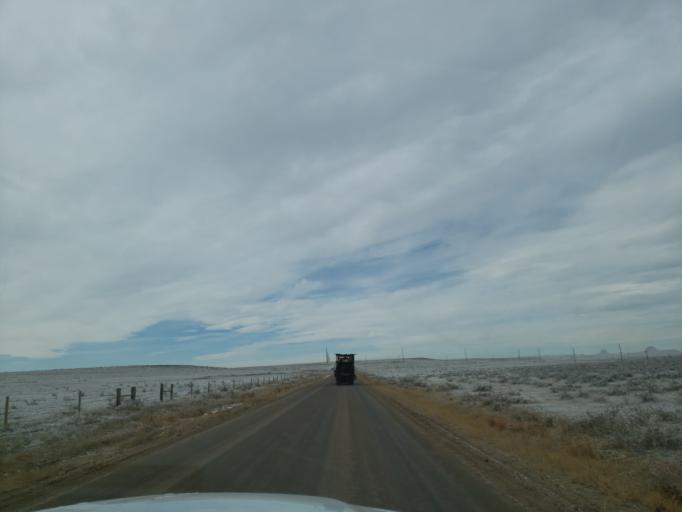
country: US
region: Wyoming
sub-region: Laramie County
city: Pine Bluffs
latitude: 40.7877
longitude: -103.8842
